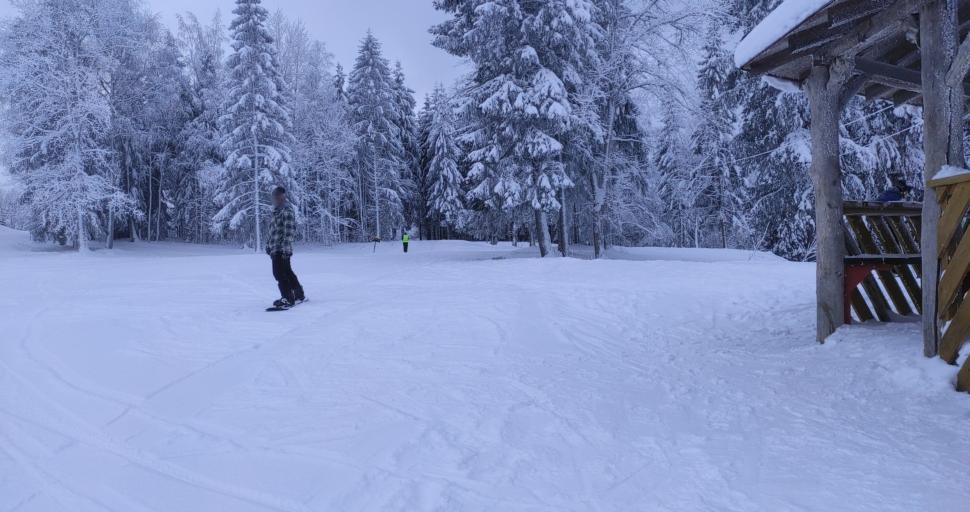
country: LV
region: Vecpiebalga
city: Vecpiebalga
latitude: 56.8746
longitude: 25.9634
